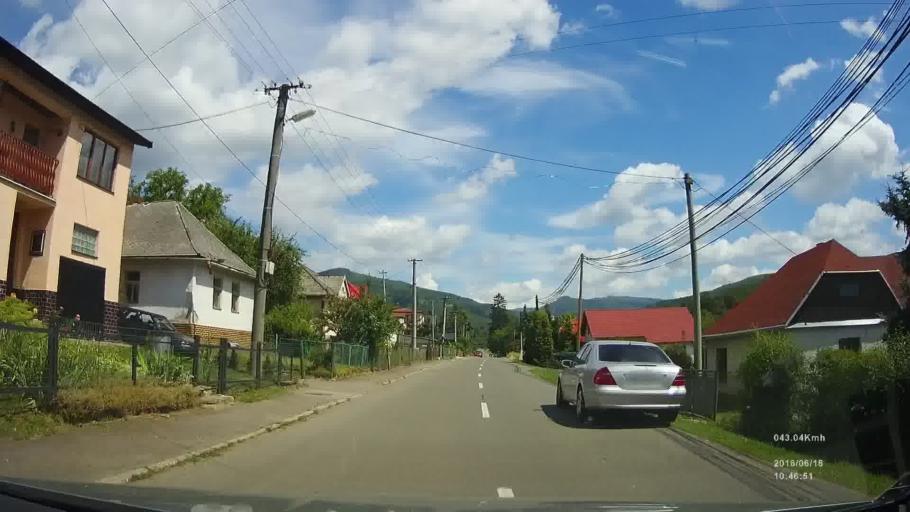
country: SK
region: Kosicky
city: Sobrance
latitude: 48.8461
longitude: 22.1831
